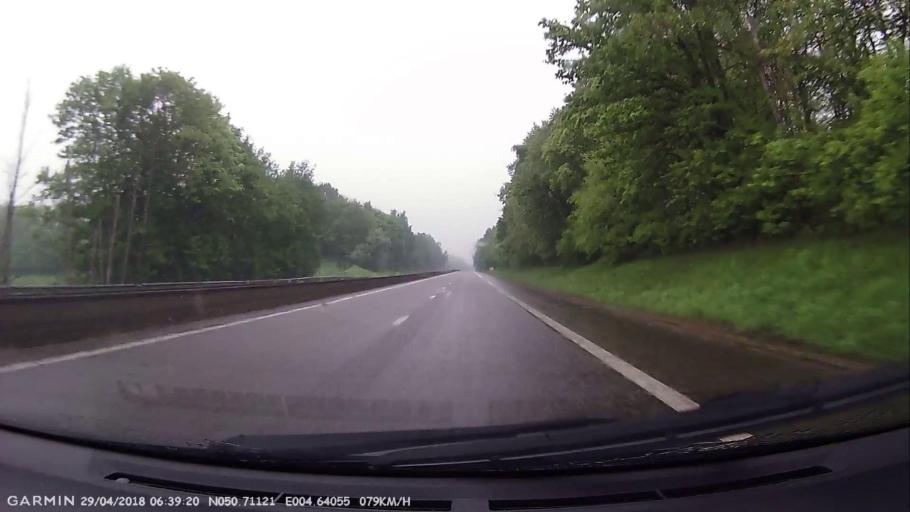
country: BE
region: Wallonia
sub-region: Province du Brabant Wallon
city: Wavre
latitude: 50.7115
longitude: 4.6407
